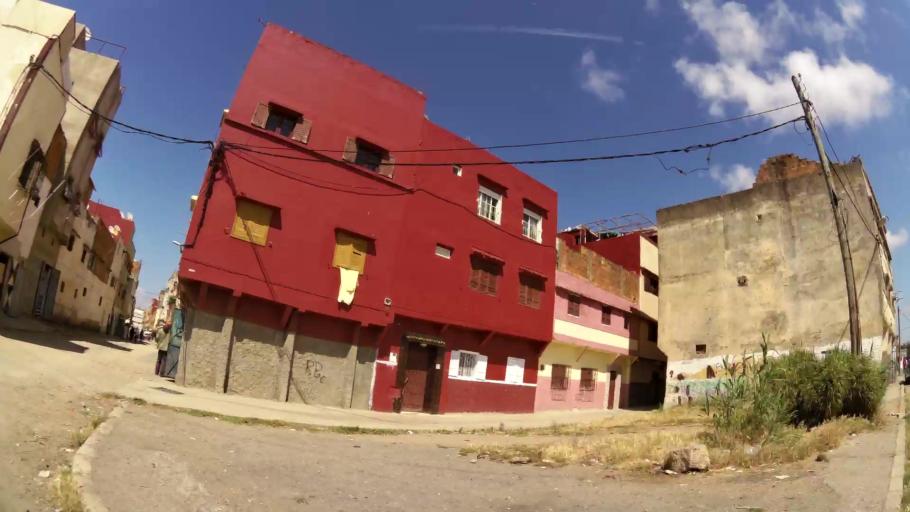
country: MA
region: Rabat-Sale-Zemmour-Zaer
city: Sale
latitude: 34.0363
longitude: -6.7992
